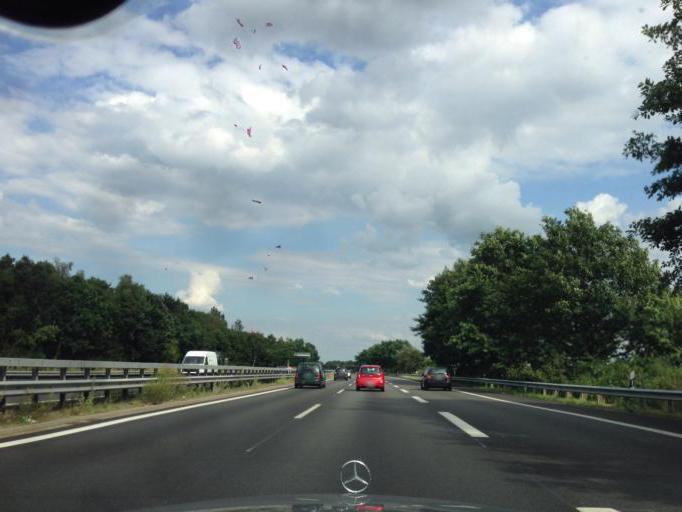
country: DE
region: Hamburg
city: Bergedorf
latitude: 53.4732
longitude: 10.1803
